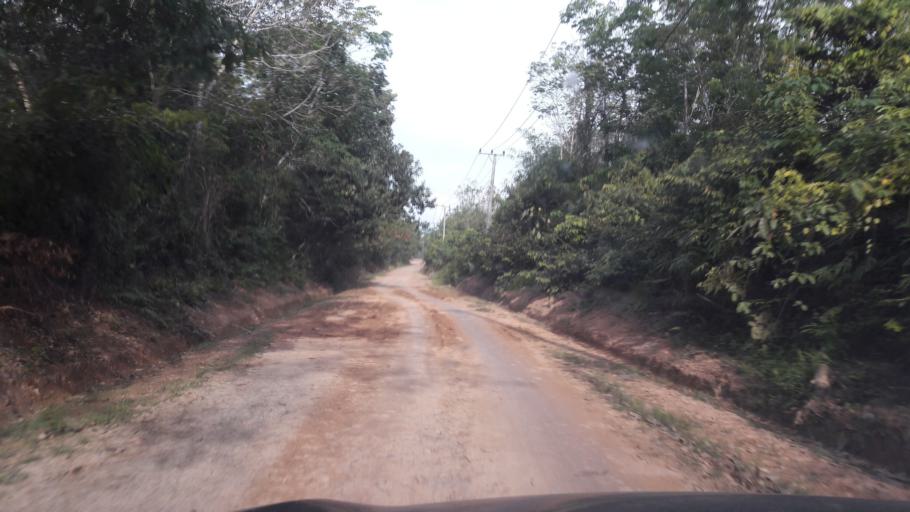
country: ID
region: South Sumatra
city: Gunungmenang
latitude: -3.2496
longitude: 104.0147
